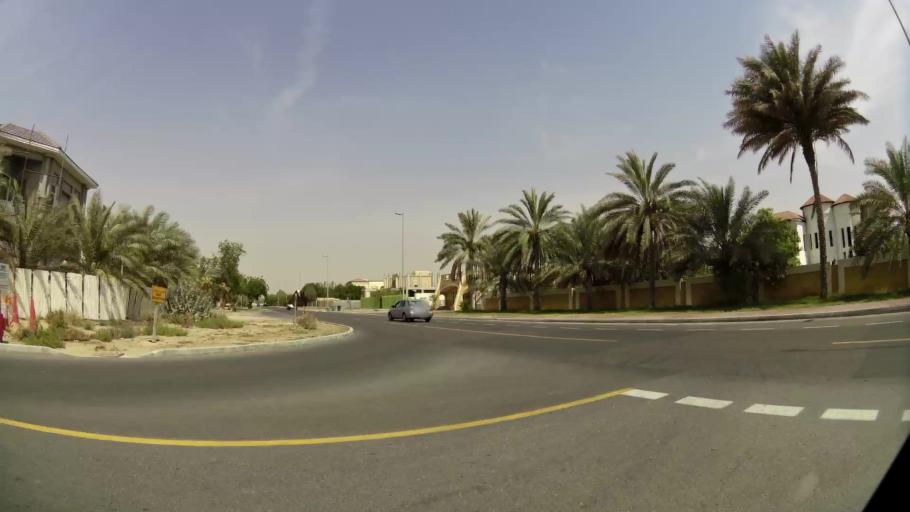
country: AE
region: Ash Shariqah
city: Sharjah
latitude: 25.2384
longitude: 55.4461
